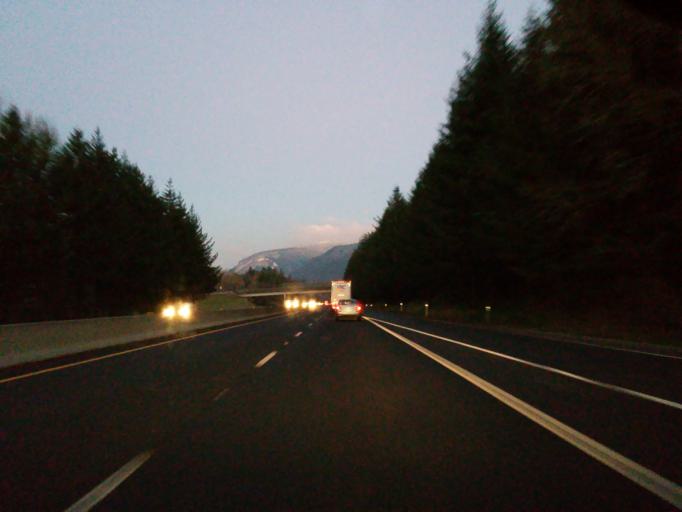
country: US
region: Washington
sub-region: Clark County
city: Washougal
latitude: 45.5438
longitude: -122.2398
